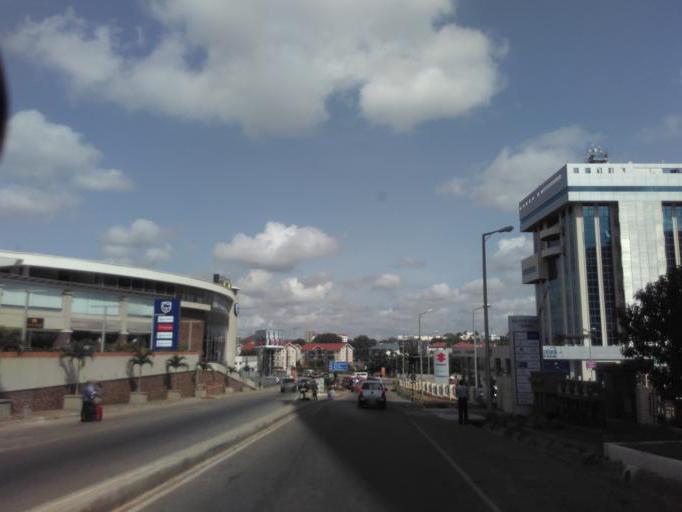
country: GH
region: Greater Accra
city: Accra
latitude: 5.5996
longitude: -0.1774
